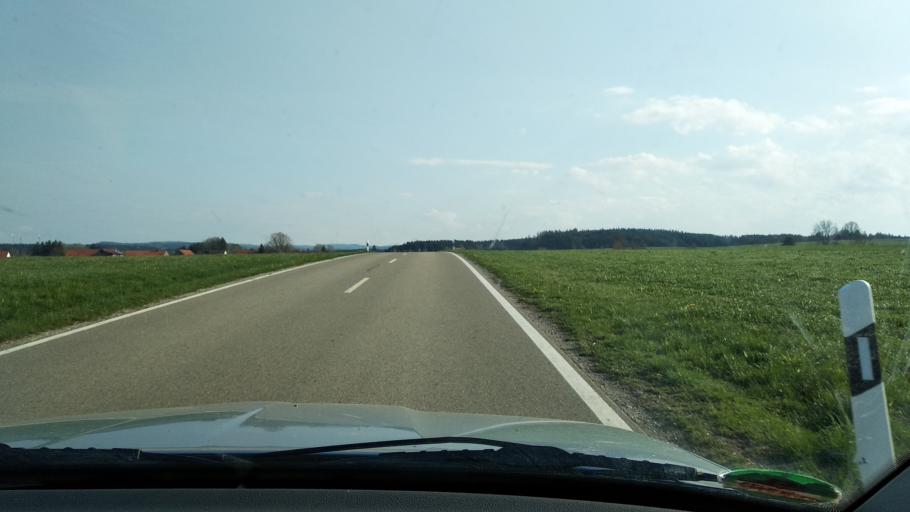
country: DE
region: Bavaria
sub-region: Swabia
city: Legau
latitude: 47.8393
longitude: 10.0899
